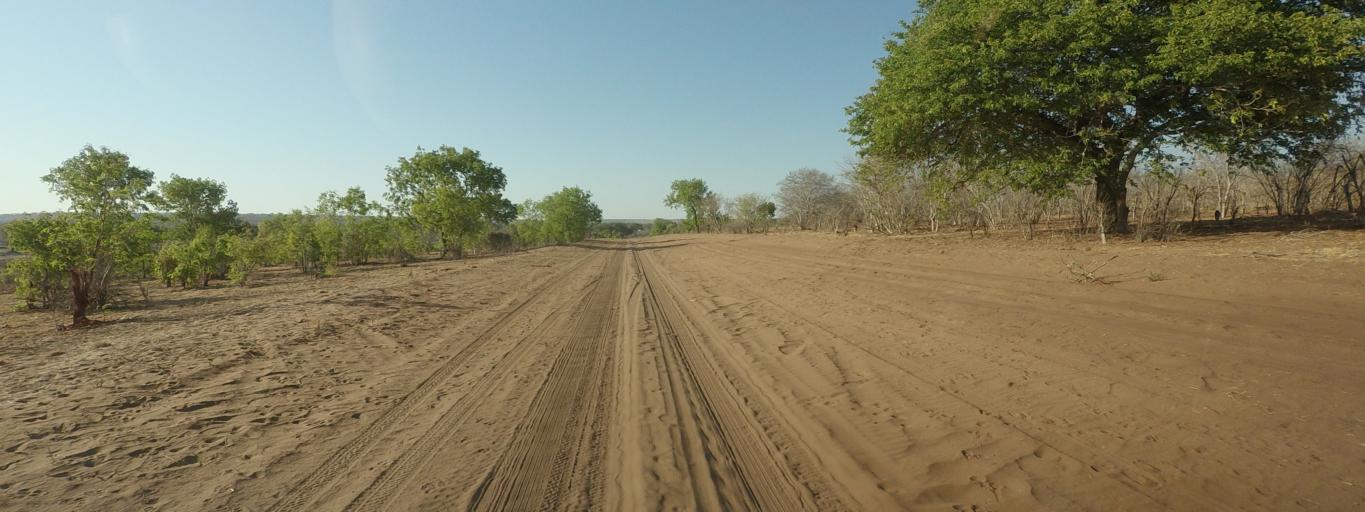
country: BW
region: North West
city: Kasane
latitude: -17.8750
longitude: 25.2343
